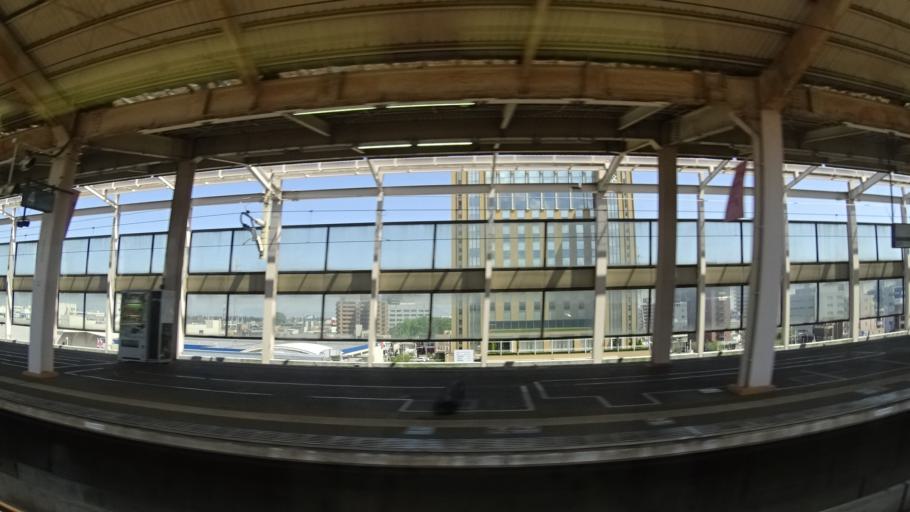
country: JP
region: Tochigi
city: Oyama
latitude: 36.3128
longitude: 139.8063
